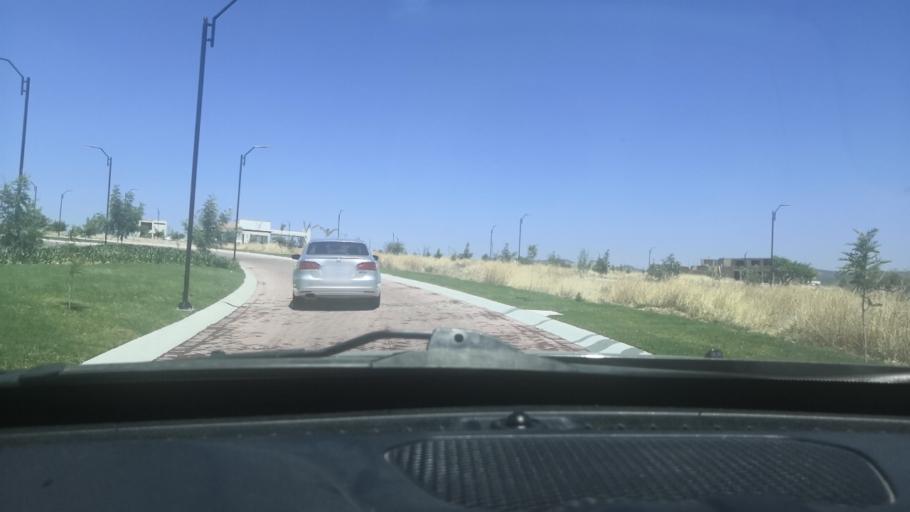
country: MX
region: Guanajuato
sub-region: Leon
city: Fraccionamiento Paseo de las Torres
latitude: 21.2305
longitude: -101.8114
